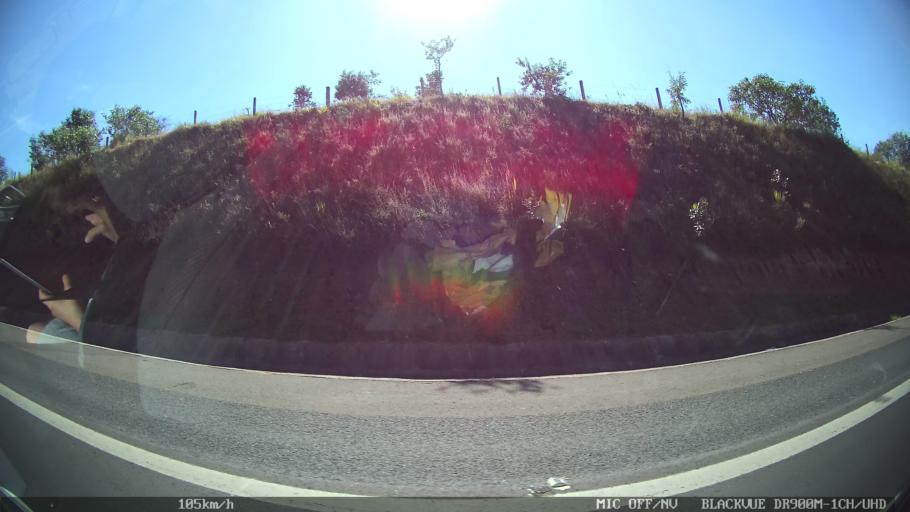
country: BR
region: Sao Paulo
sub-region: Franca
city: Franca
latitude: -20.5545
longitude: -47.4273
